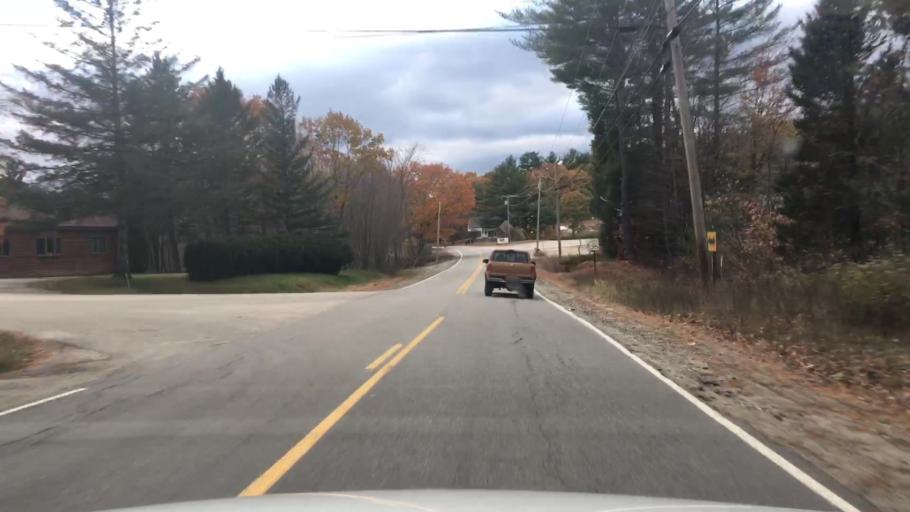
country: US
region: Maine
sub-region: Androscoggin County
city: Livermore
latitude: 44.3402
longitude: -70.2462
